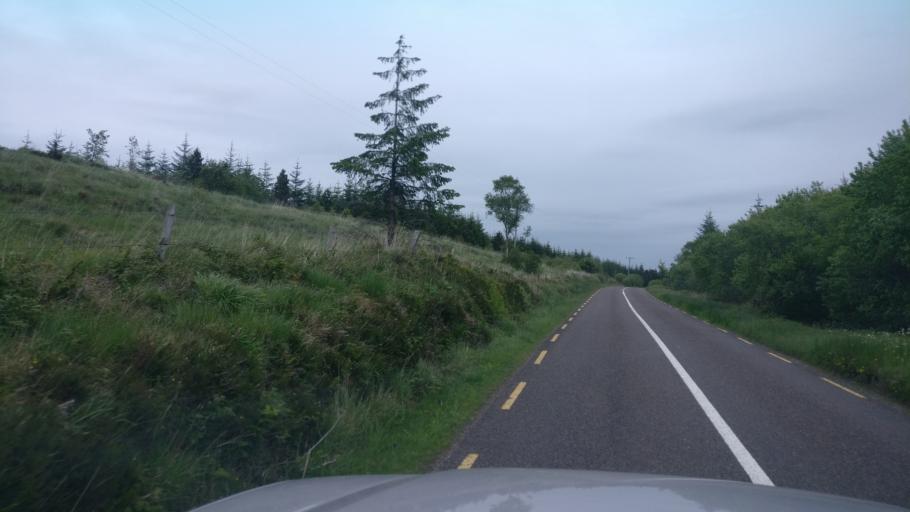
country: IE
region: Connaught
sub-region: County Galway
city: Loughrea
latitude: 53.0732
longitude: -8.5758
